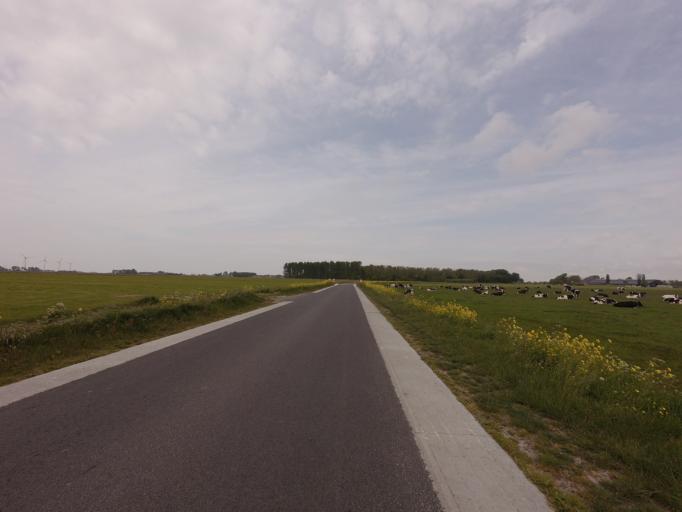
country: NL
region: Friesland
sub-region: Sudwest Fryslan
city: Bolsward
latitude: 53.0911
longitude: 5.4792
